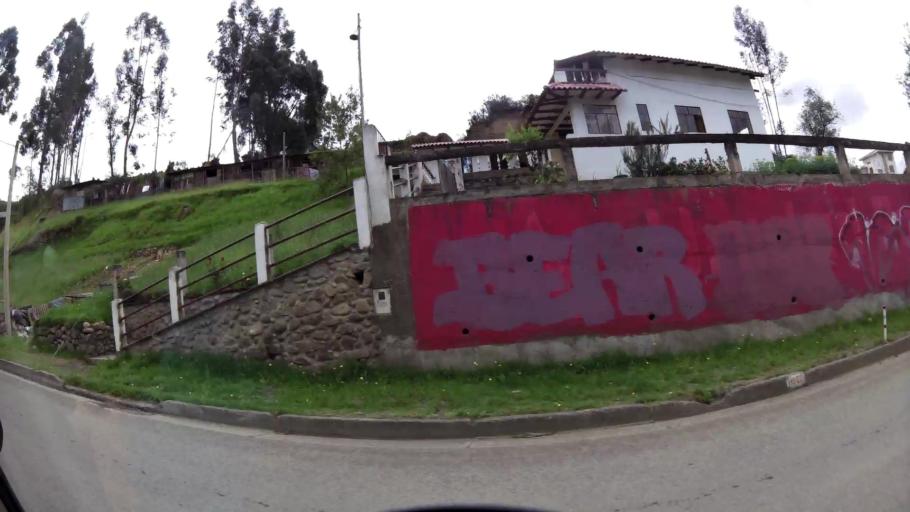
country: EC
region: Azuay
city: Cuenca
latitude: -2.8998
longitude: -79.0475
